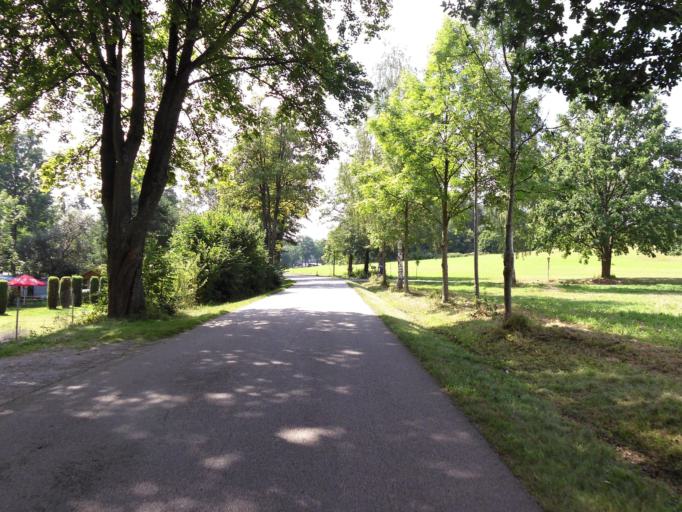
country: CZ
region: Jihocesky
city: Chlum u Trebone
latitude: 48.9658
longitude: 14.9377
